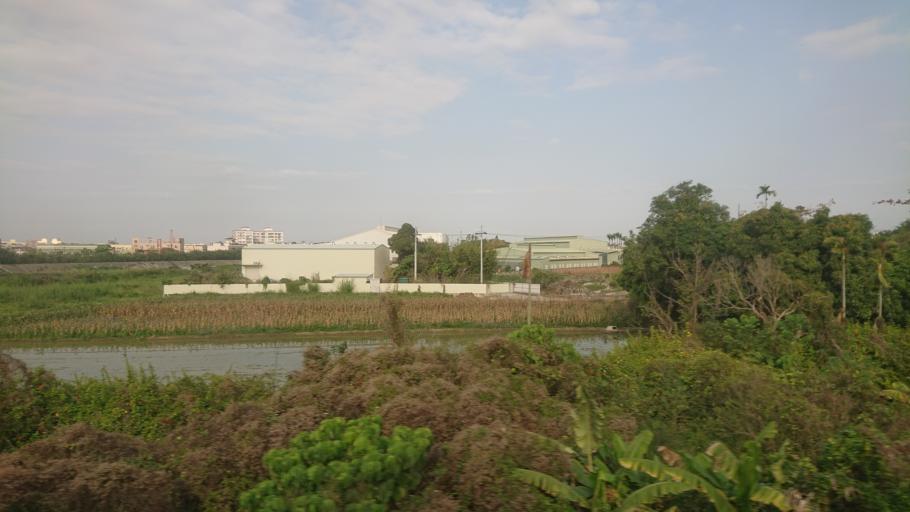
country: TW
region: Taiwan
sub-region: Yunlin
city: Douliu
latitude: 23.6820
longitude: 120.4889
